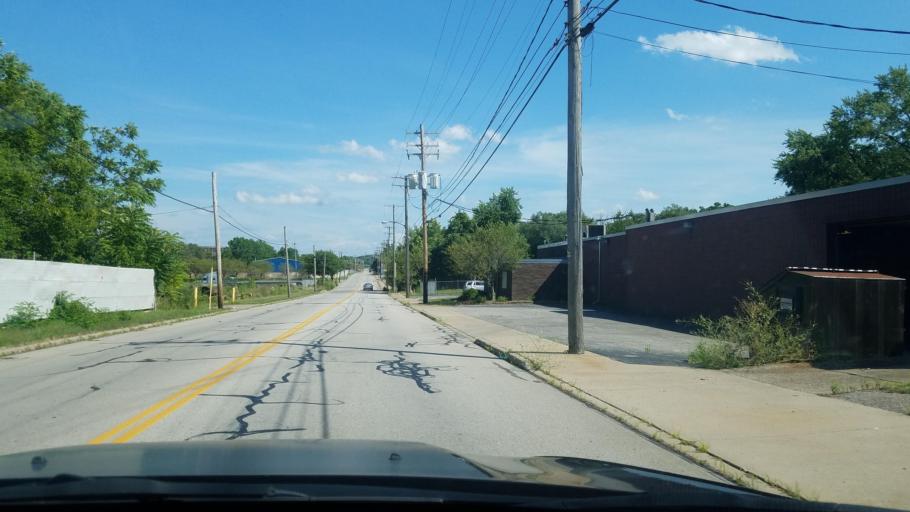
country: US
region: Ohio
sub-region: Mahoning County
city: Youngstown
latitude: 41.0841
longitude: -80.6346
